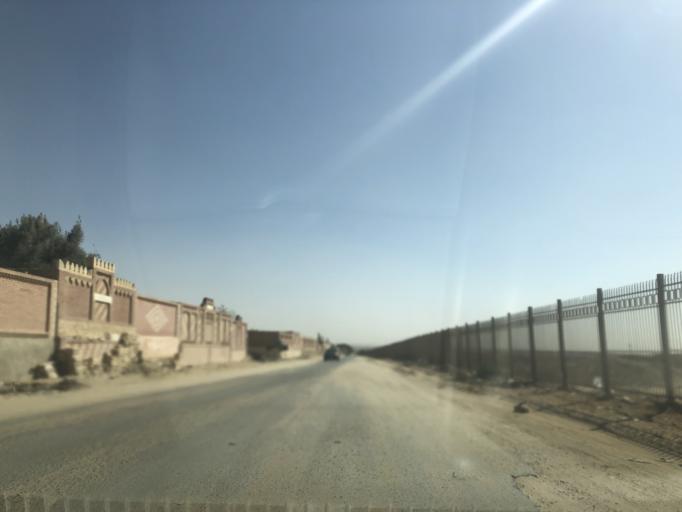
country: EG
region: Al Jizah
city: Madinat Sittah Uktubar
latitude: 29.9307
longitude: 30.9543
